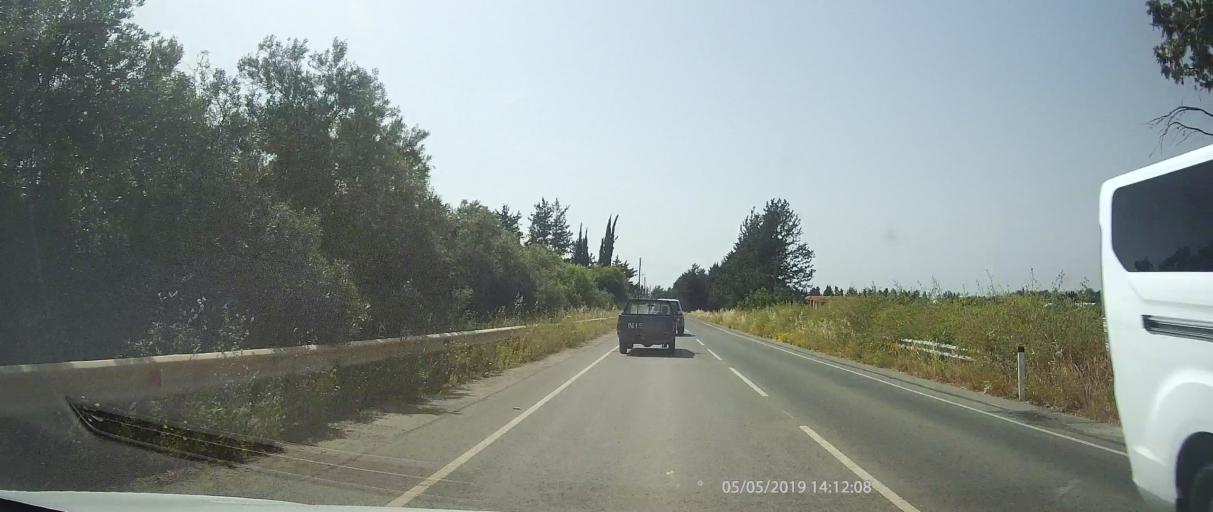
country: CY
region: Pafos
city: Mesogi
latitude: 34.7184
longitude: 32.5408
